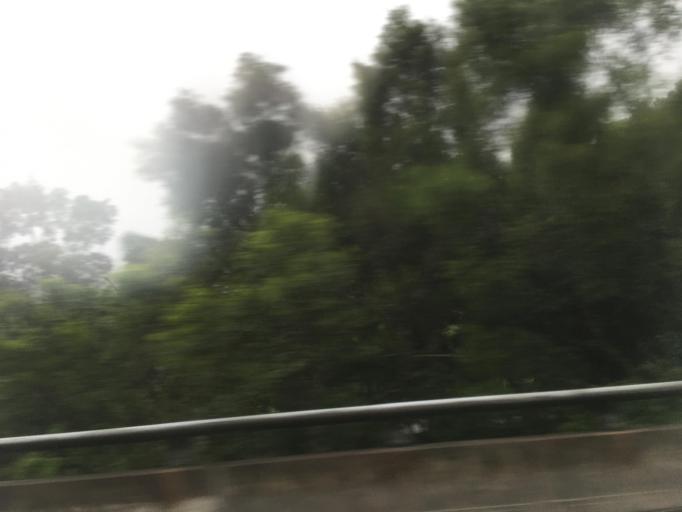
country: TW
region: Taipei
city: Taipei
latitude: 24.9795
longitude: 121.6753
